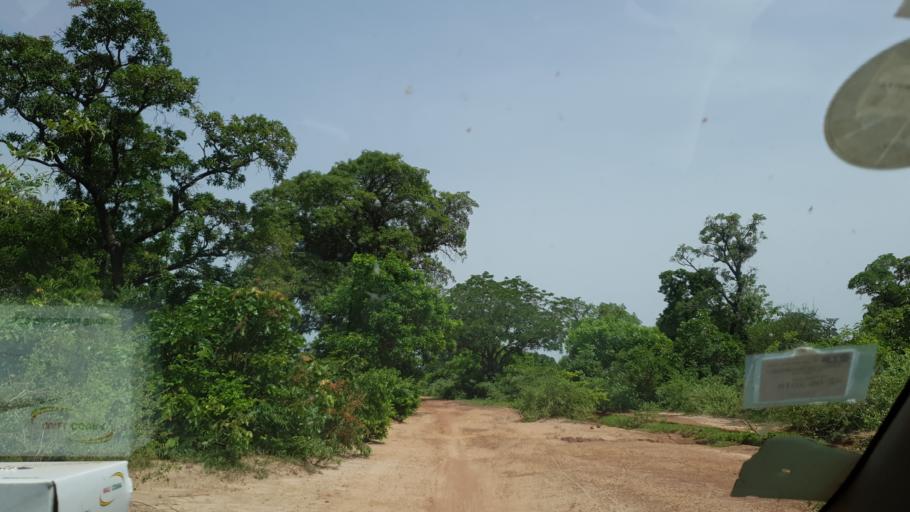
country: ML
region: Koulikoro
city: Koulikoro
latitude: 12.6678
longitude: -7.2416
